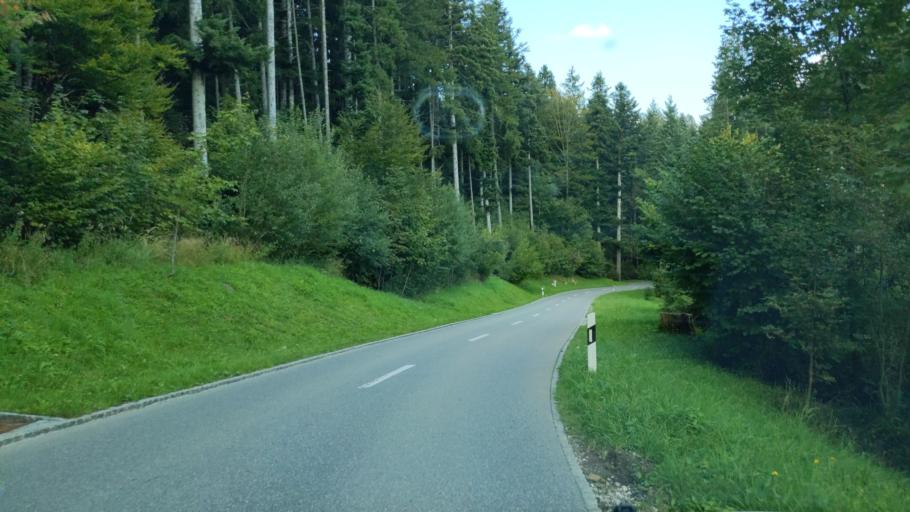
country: CH
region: Saint Gallen
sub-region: Wahlkreis Rheintal
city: Eichberg
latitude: 47.3449
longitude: 9.5032
